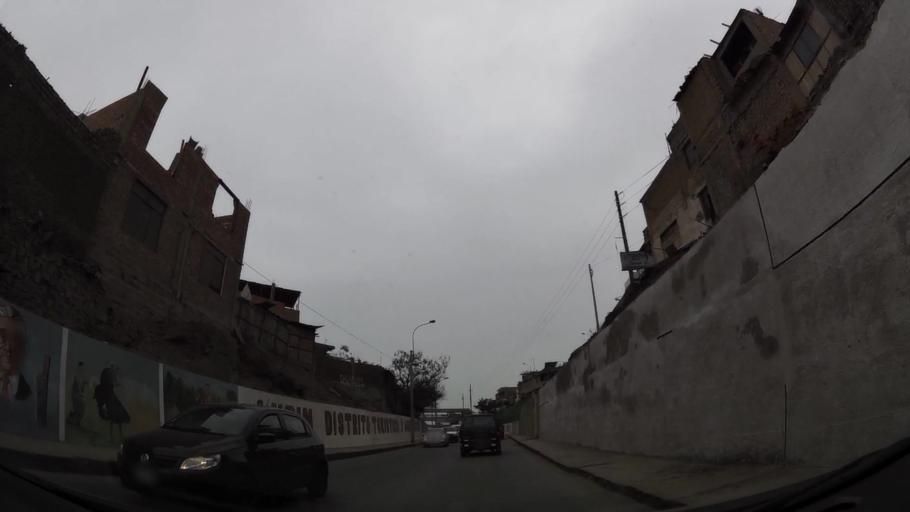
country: PE
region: Lima
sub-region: Lima
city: Punta Hermosa
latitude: -12.2525
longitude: -76.8953
